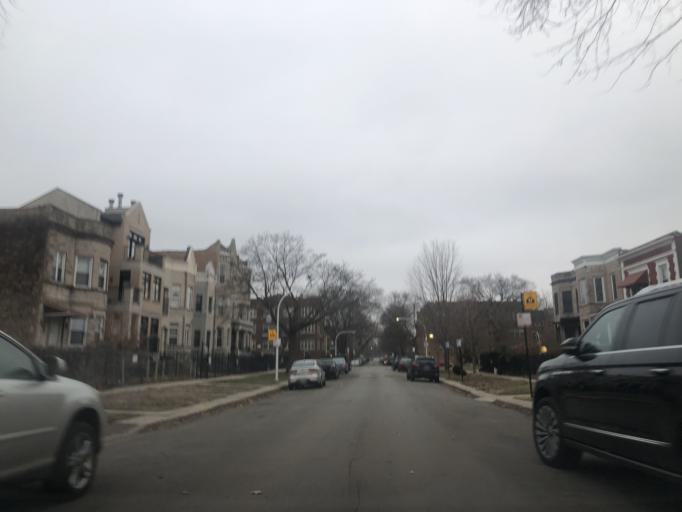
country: US
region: Illinois
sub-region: Cook County
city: Chicago
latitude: 41.7760
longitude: -87.6022
